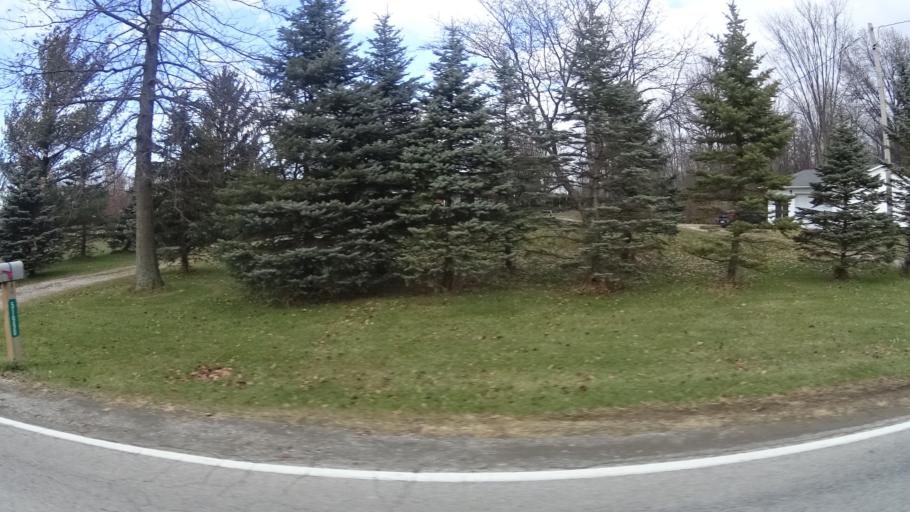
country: US
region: Ohio
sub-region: Lorain County
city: Camden
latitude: 41.2761
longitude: -82.3268
